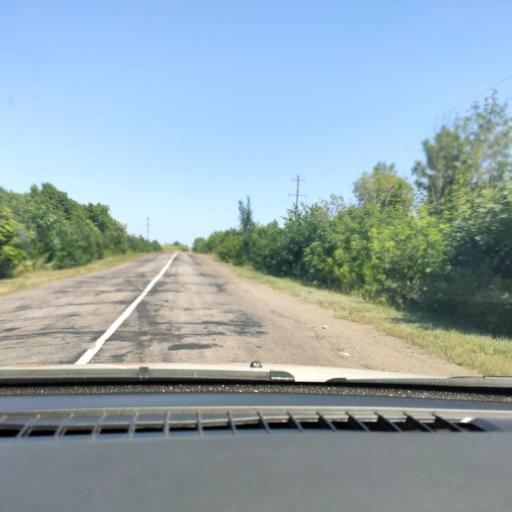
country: RU
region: Voronezj
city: Ol'khovatka
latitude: 50.6039
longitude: 39.3133
